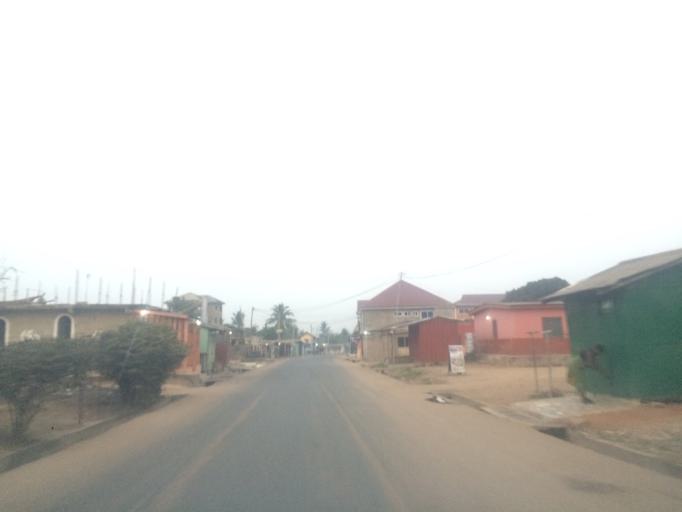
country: GH
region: Greater Accra
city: Nungua
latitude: 5.6044
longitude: -0.0881
